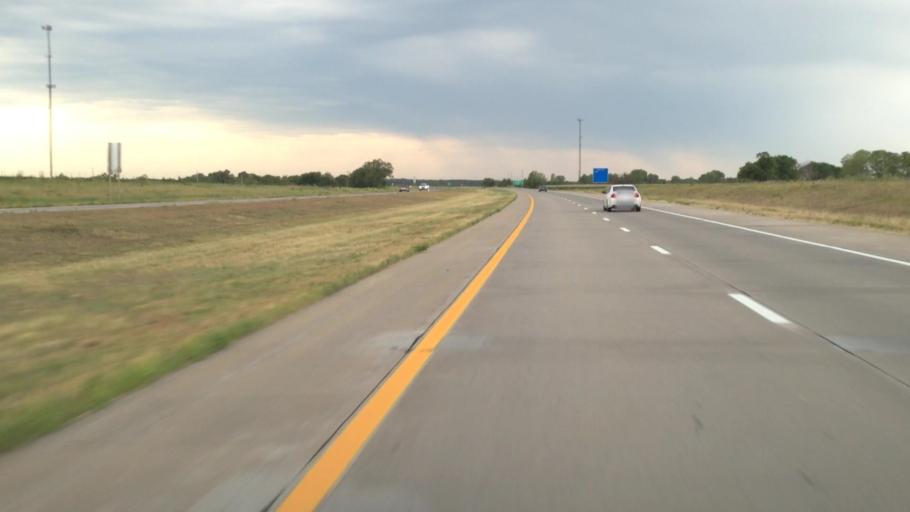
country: US
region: Kansas
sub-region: Franklin County
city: Ottawa
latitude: 38.4953
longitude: -95.4630
